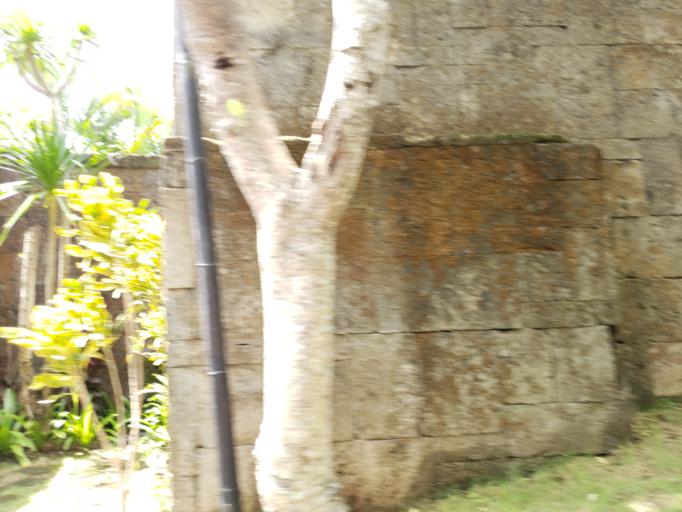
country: ID
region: Bali
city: Pecatu
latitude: -8.8443
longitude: 115.1191
